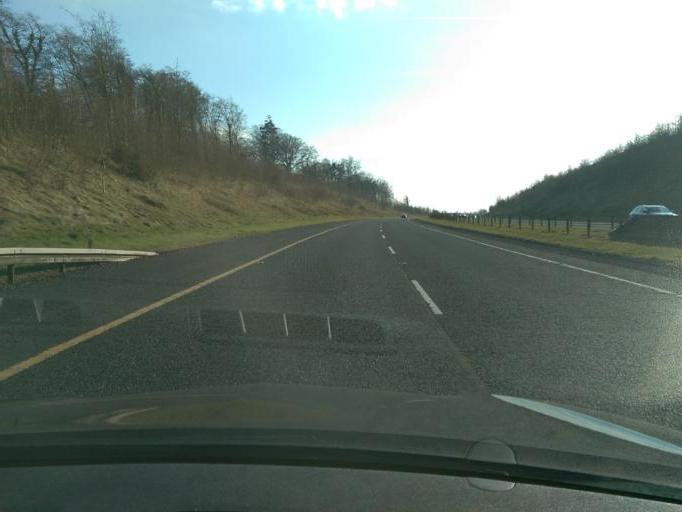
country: IE
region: Leinster
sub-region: Kildare
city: Monasterevin
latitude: 53.1218
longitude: -7.0408
